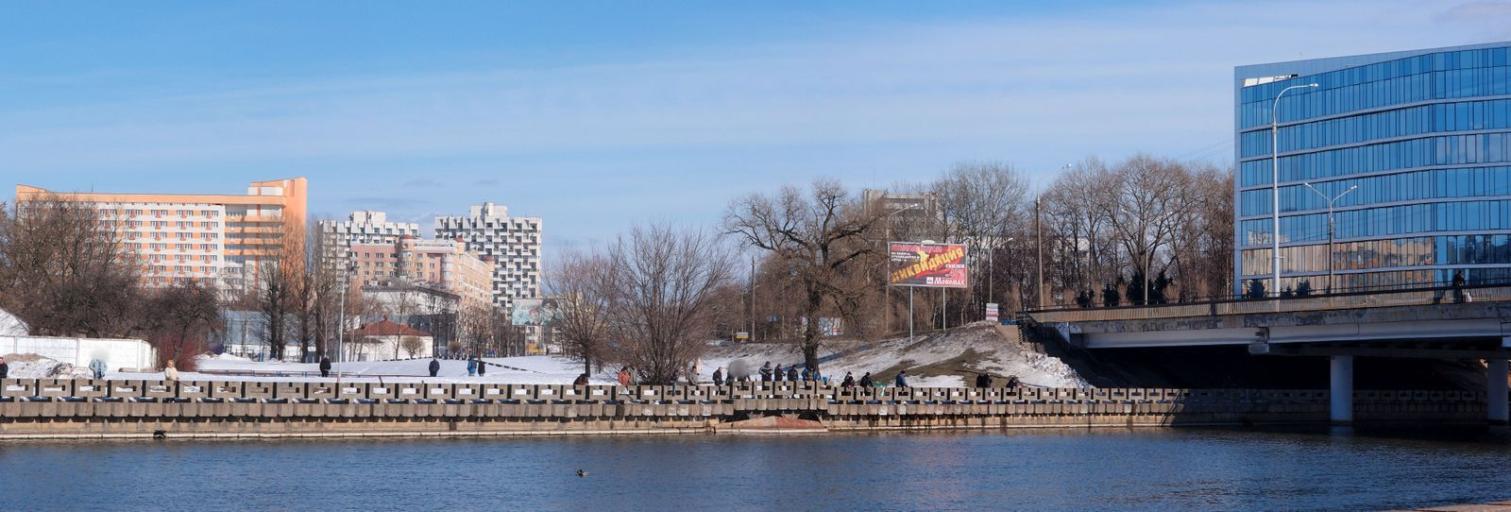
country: BY
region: Minsk
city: Minsk
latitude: 53.9181
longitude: 27.5467
